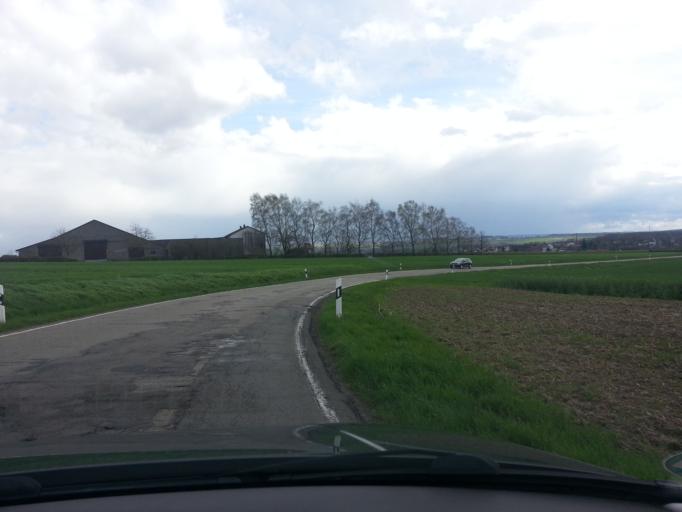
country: DE
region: Rheinland-Pfalz
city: Massweiler
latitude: 49.2790
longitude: 7.5258
